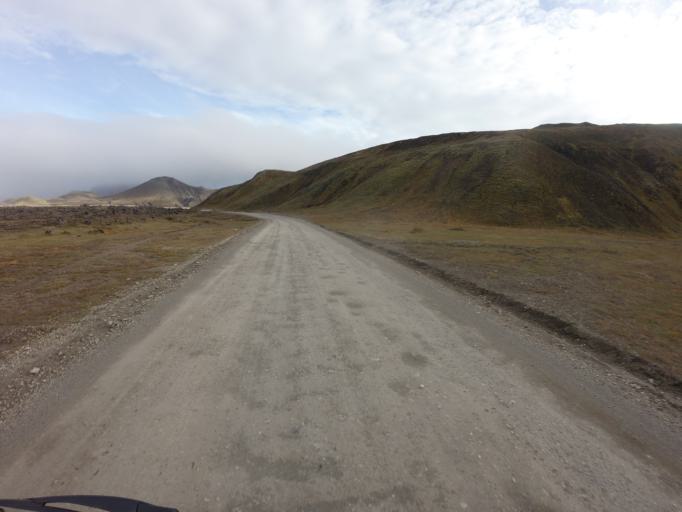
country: IS
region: South
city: Vestmannaeyjar
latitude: 64.0073
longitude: -19.0413
